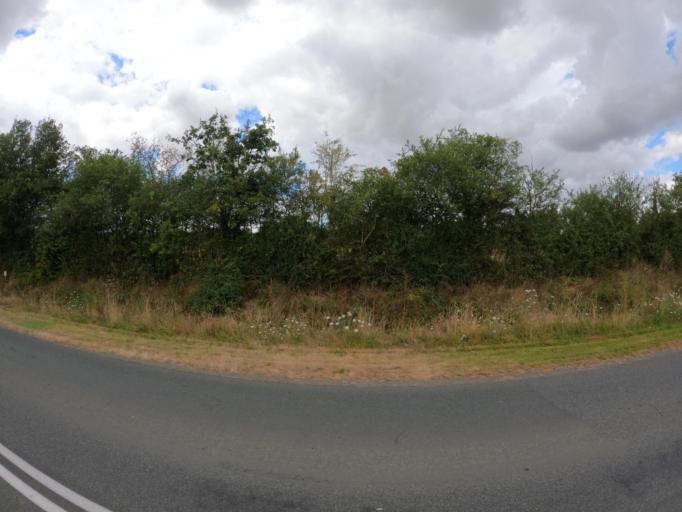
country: FR
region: Pays de la Loire
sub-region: Departement de Maine-et-Loire
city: Morannes
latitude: 47.8036
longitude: -0.4256
